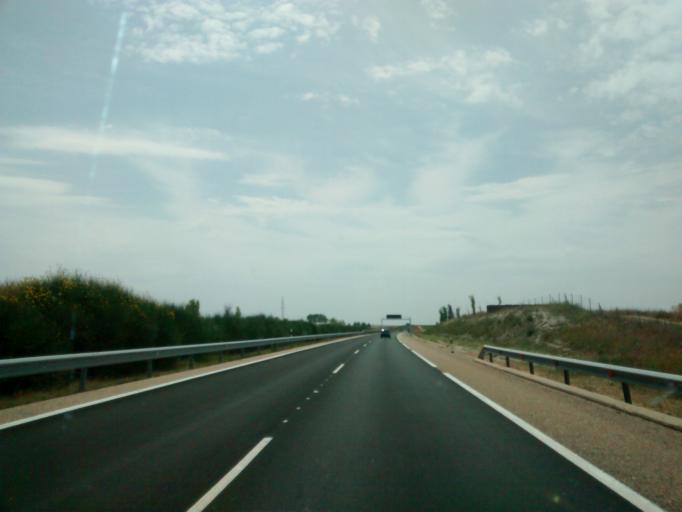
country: ES
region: Castille and Leon
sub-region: Provincia de Burgos
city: Villalbilla de Burgos
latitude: 42.3218
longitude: -3.7665
